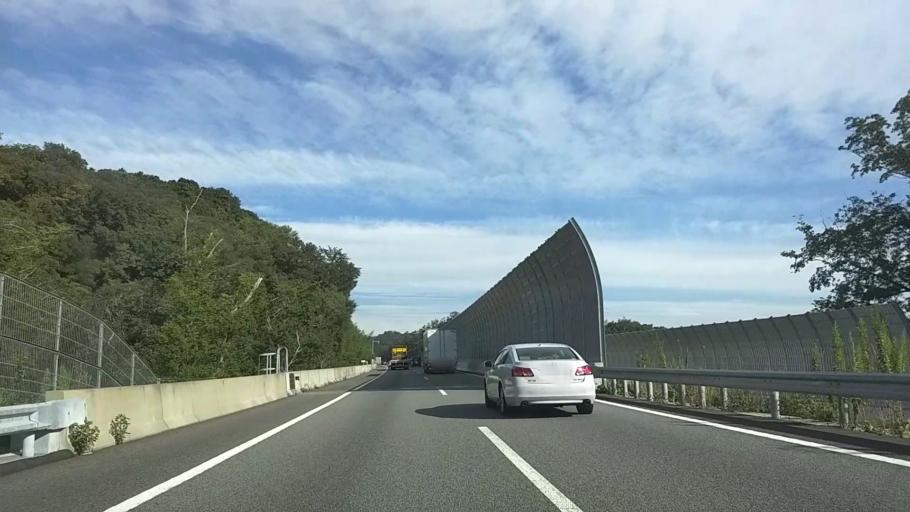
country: JP
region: Kanagawa
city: Zama
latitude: 35.5500
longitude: 139.3183
